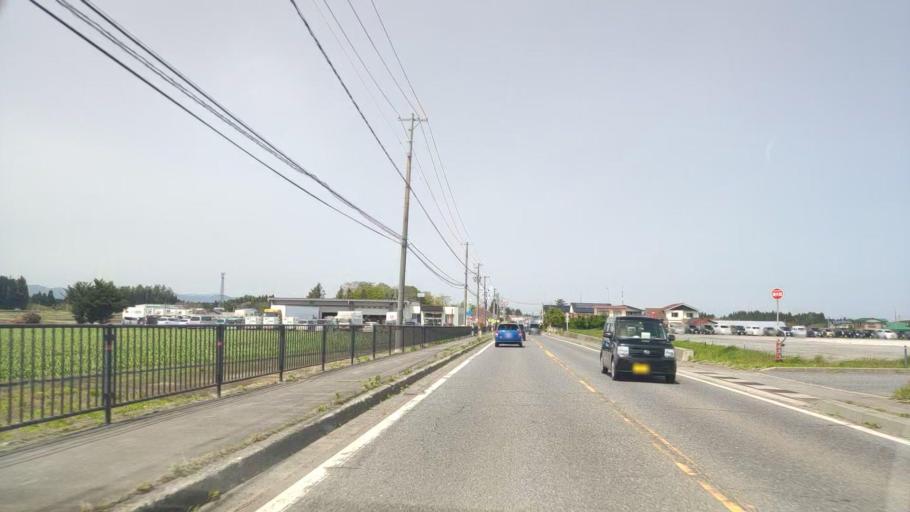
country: JP
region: Aomori
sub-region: Misawa Shi
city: Inuotose
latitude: 40.6517
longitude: 141.1953
